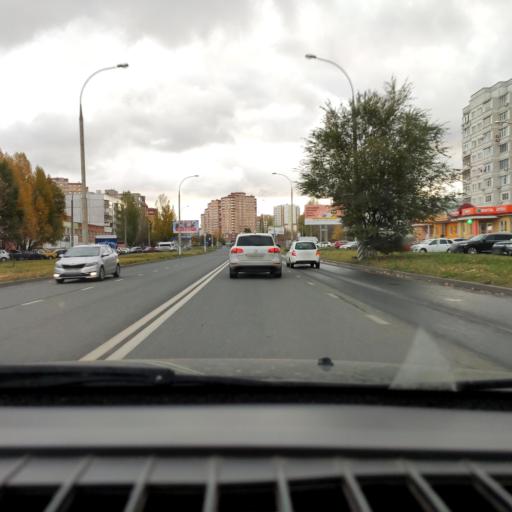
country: RU
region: Samara
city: Tol'yatti
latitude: 53.5435
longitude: 49.3609
